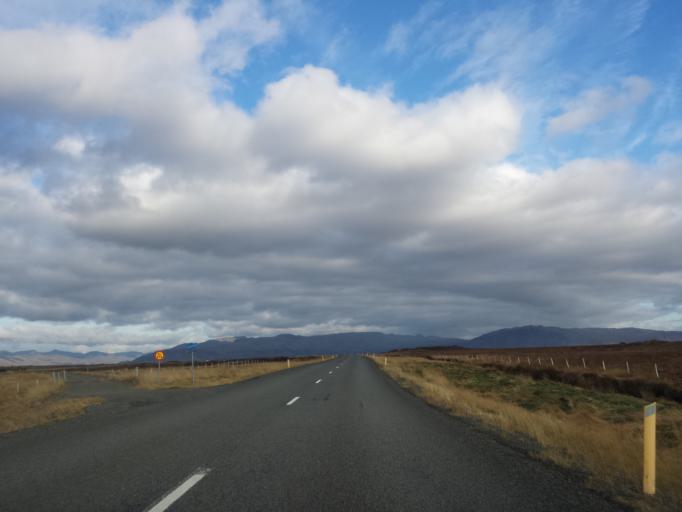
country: IS
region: West
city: Borgarnes
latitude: 64.6427
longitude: -22.0669
